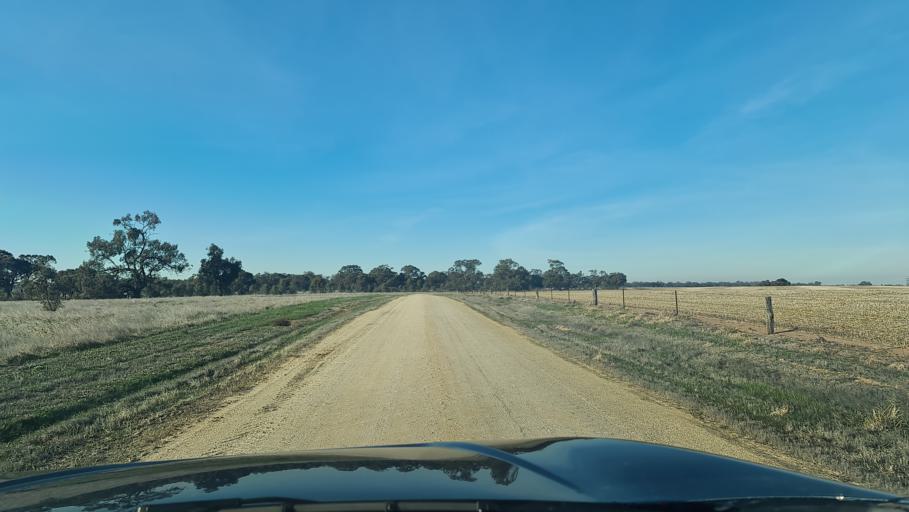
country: AU
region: Victoria
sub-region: Horsham
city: Horsham
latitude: -36.3553
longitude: 142.3953
